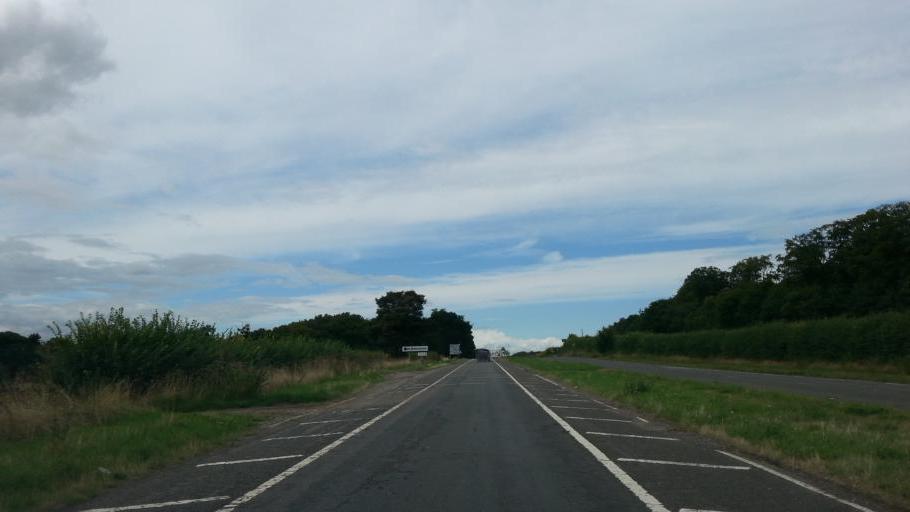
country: GB
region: England
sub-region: Cambridgeshire
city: Sawston
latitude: 52.1321
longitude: 0.2162
